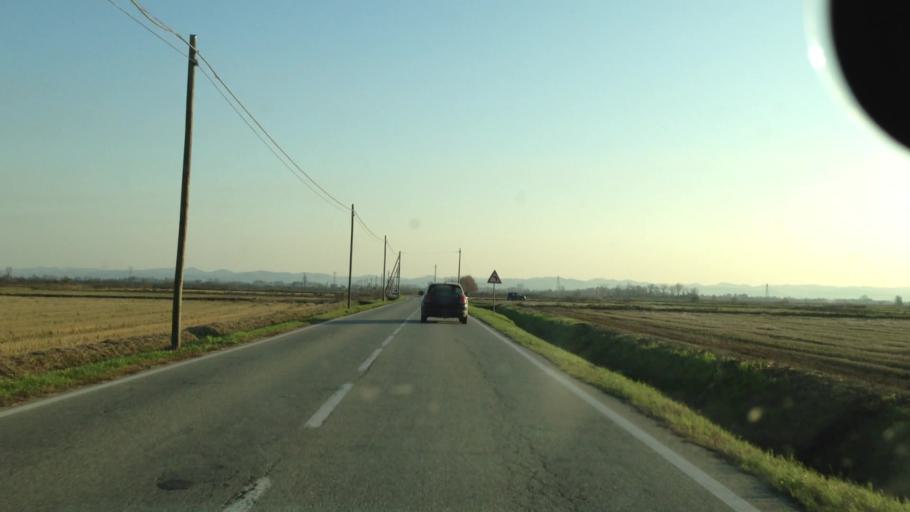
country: IT
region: Piedmont
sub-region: Provincia di Vercelli
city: Livorno Ferraris
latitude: 45.2611
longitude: 8.0843
